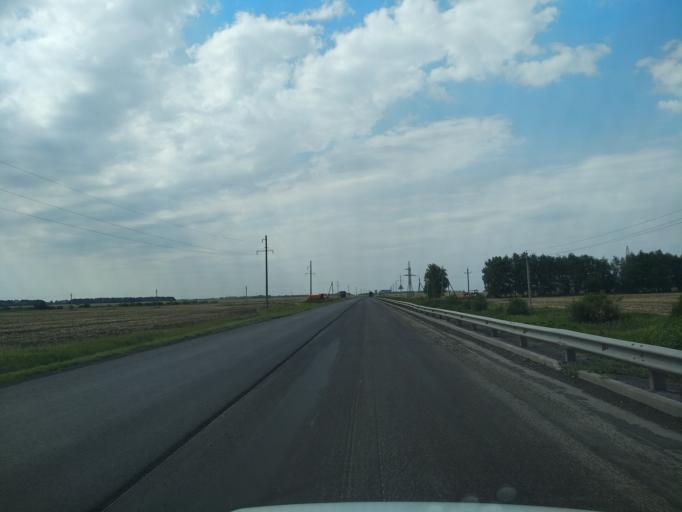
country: RU
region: Voronezj
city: Pereleshino
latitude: 51.7945
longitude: 40.1487
